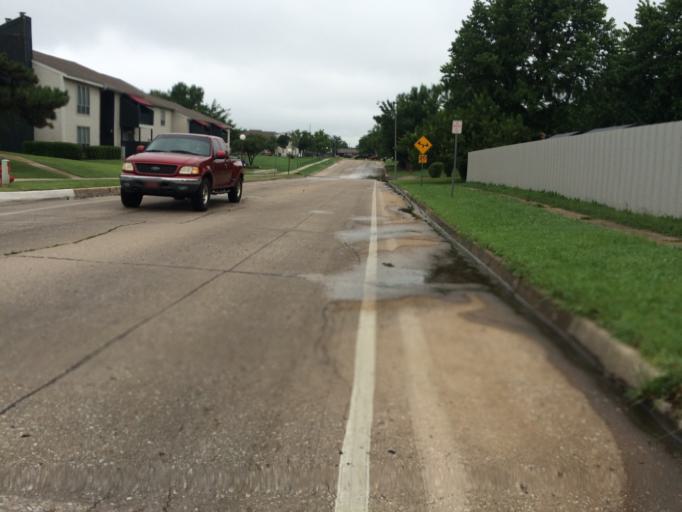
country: US
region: Oklahoma
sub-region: Cleveland County
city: Norman
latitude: 35.2080
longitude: -97.4192
